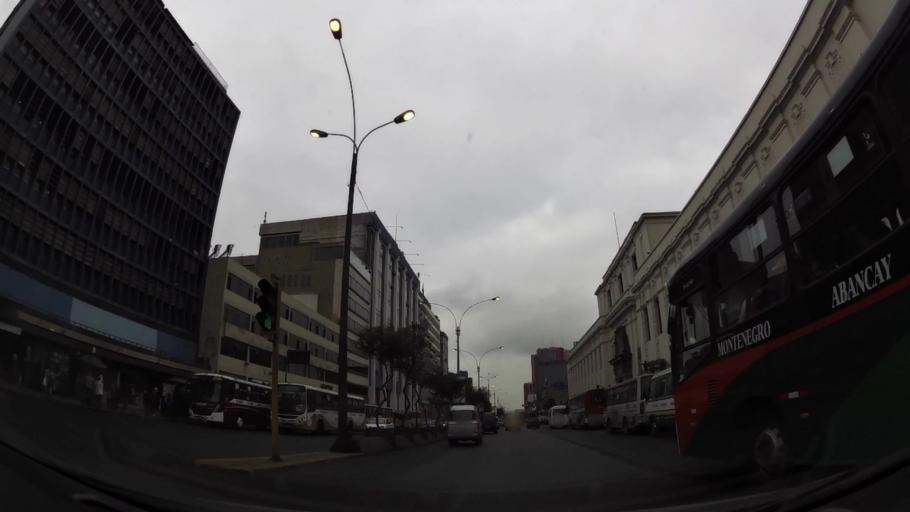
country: PE
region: Lima
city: Lima
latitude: -12.0498
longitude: -77.0278
